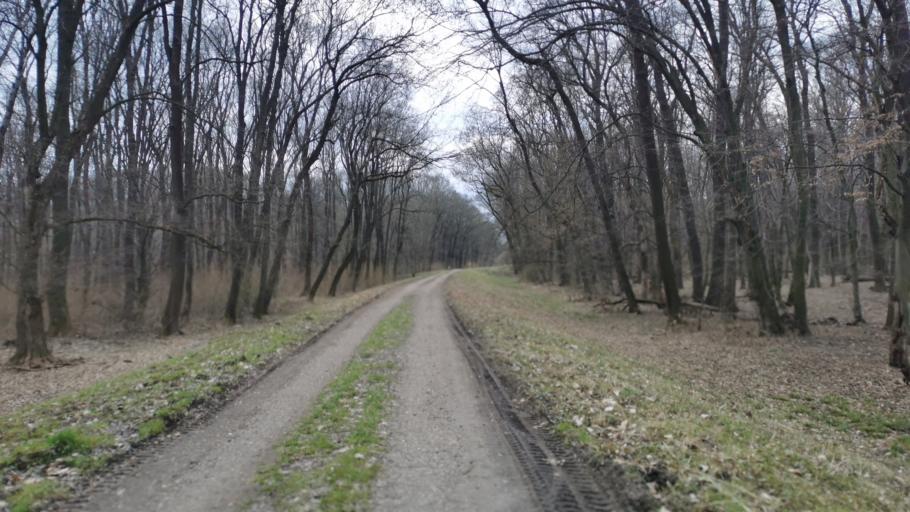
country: CZ
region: South Moravian
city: Rohatec
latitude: 48.8563
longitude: 17.1789
